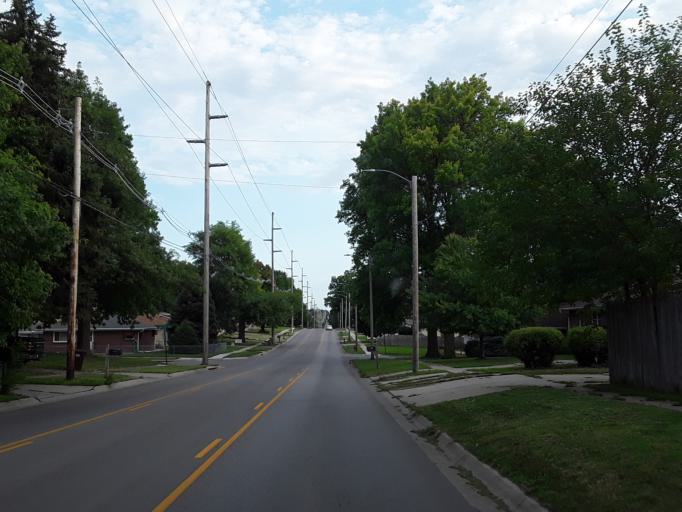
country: US
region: Nebraska
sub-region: Lancaster County
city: Lincoln
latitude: 40.8342
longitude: -96.6442
